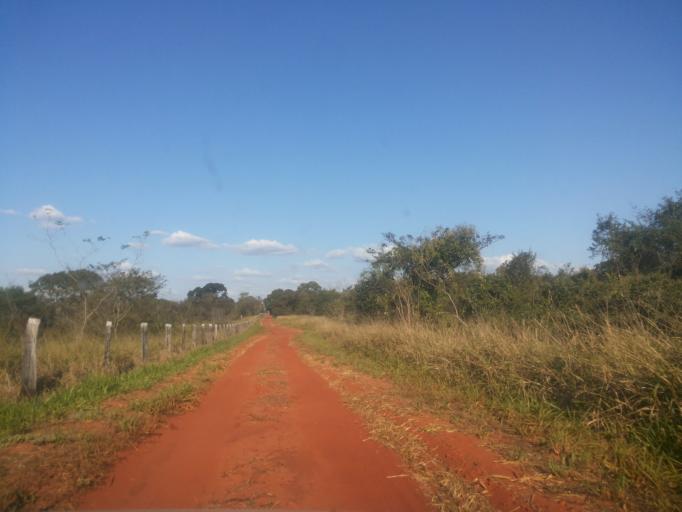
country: BR
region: Minas Gerais
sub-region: Santa Vitoria
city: Santa Vitoria
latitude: -19.0158
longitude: -50.4483
